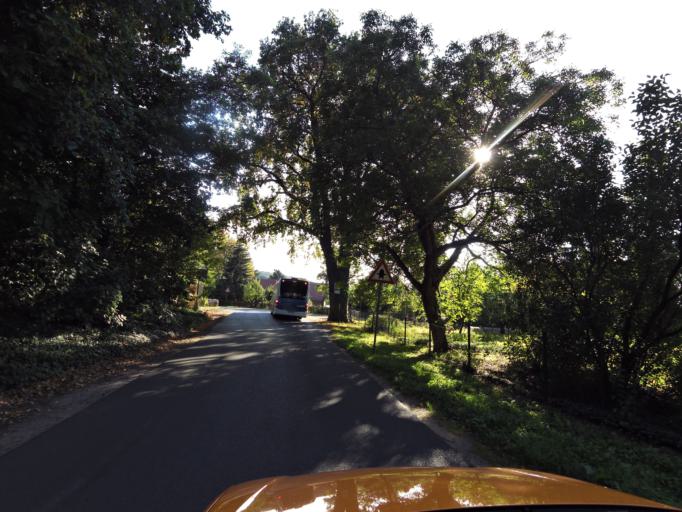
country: DE
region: Brandenburg
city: Potsdam
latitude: 52.4579
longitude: 13.0595
